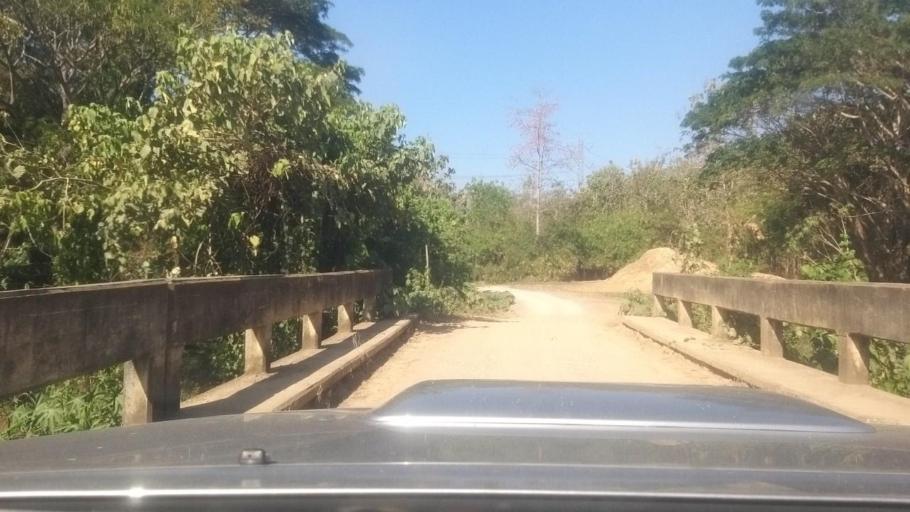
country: TH
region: Phrae
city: Nong Muang Khai
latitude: 18.3076
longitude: 100.0292
